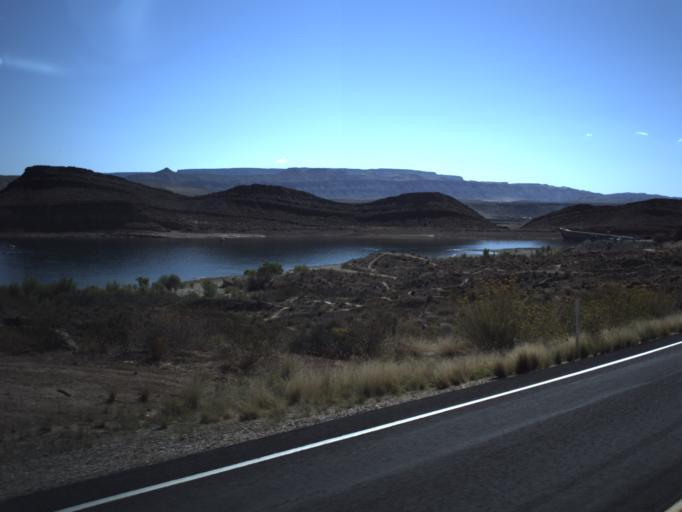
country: US
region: Utah
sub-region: Washington County
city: Hurricane
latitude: 37.1837
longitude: -113.3978
